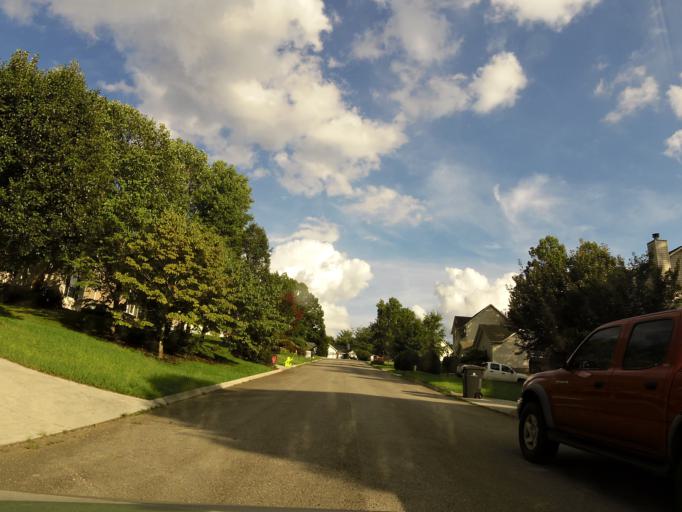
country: US
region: Tennessee
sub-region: Knox County
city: Knoxville
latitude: 36.0004
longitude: -84.0202
